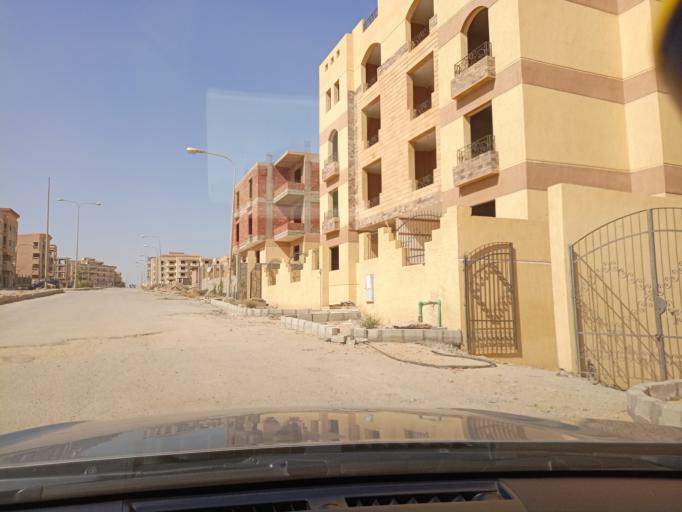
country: EG
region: Muhafazat al Qalyubiyah
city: Al Khankah
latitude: 30.2189
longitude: 31.4420
